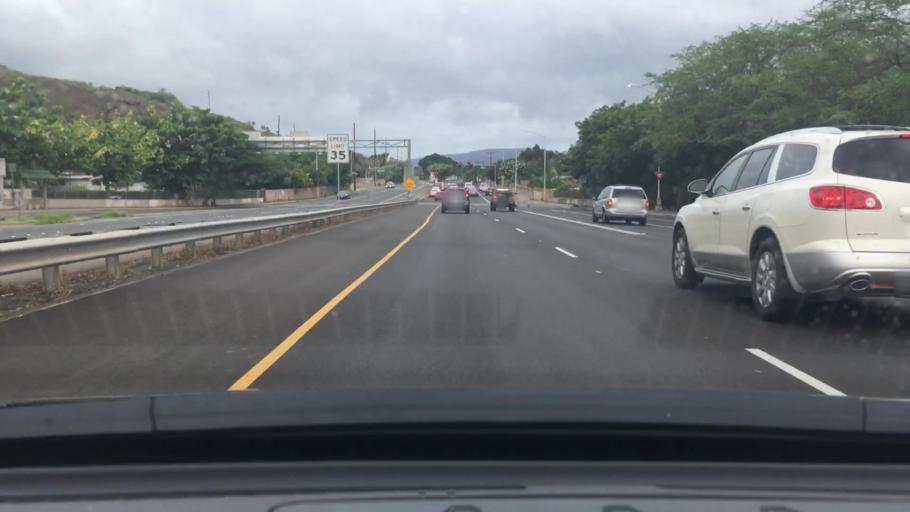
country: US
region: Hawaii
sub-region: Honolulu County
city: Honolulu
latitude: 21.2781
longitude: -157.7820
